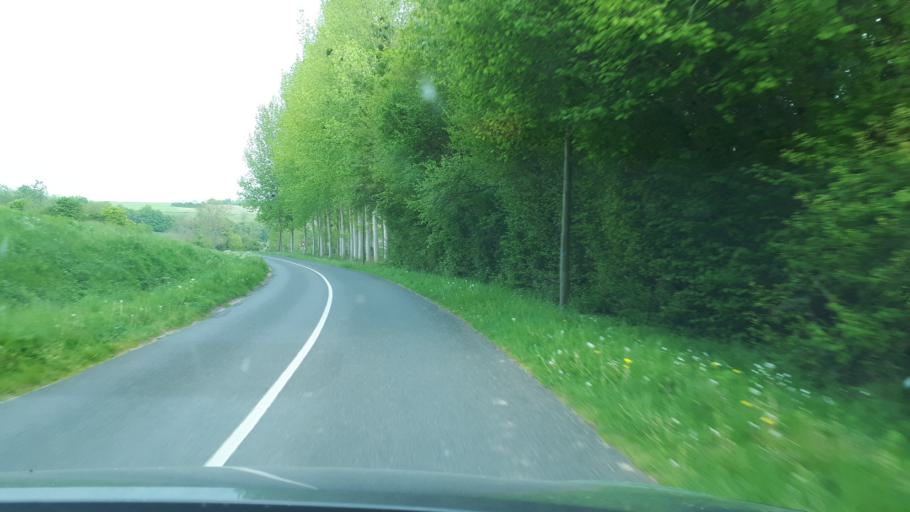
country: FR
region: Centre
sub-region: Departement du Loir-et-Cher
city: Lunay
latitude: 47.8159
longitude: 0.9544
